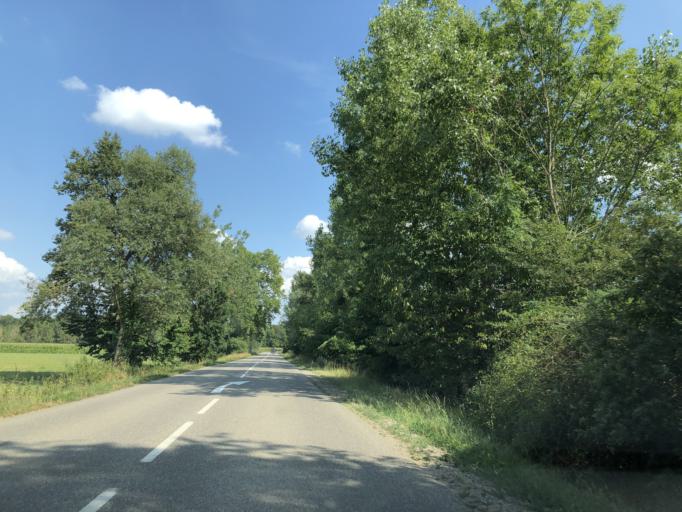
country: FR
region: Alsace
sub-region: Departement du Bas-Rhin
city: Hindisheim
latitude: 48.4400
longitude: 7.6014
